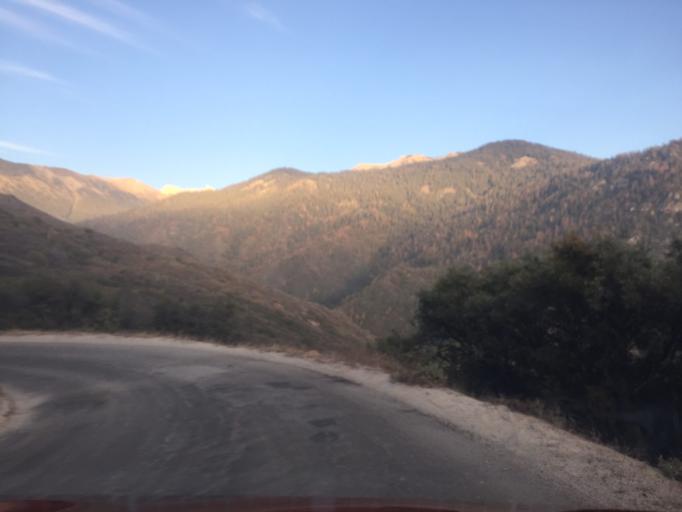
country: US
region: California
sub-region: Tulare County
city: Three Rivers
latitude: 36.4405
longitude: -118.7176
